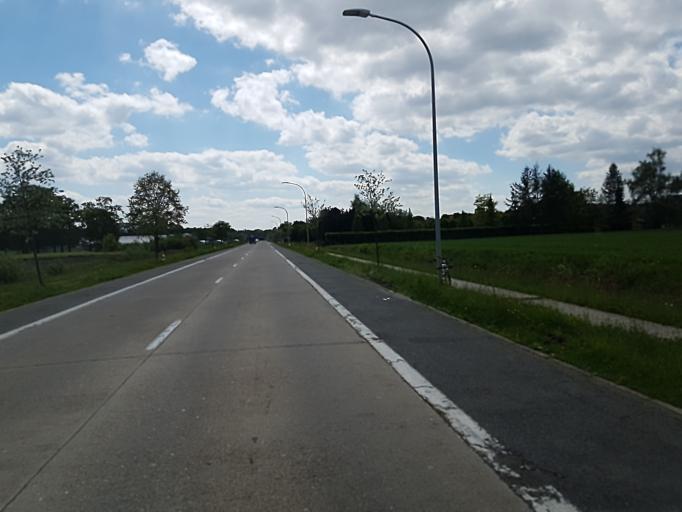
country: BE
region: Flanders
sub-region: Provincie Antwerpen
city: Westerlo
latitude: 51.0847
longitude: 4.9509
